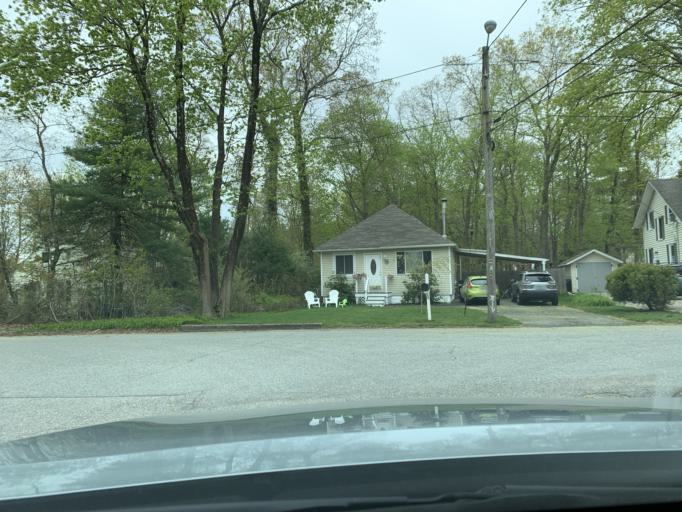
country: US
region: Rhode Island
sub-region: Kent County
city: East Greenwich
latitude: 41.6118
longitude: -71.4771
